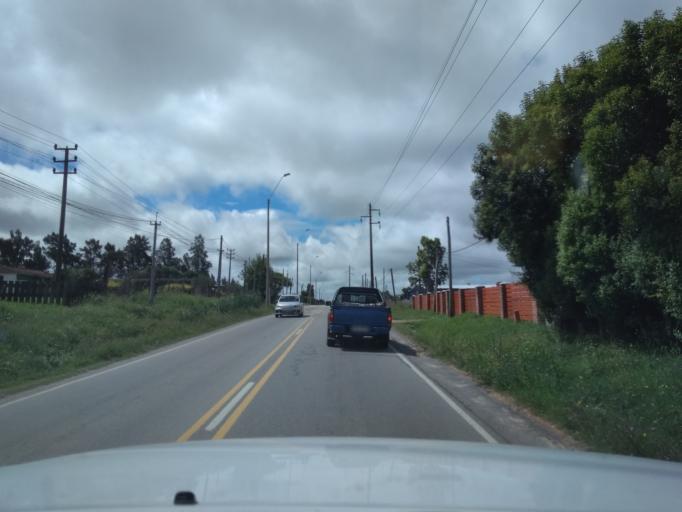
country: UY
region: Canelones
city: Pando
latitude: -34.7055
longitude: -55.9655
